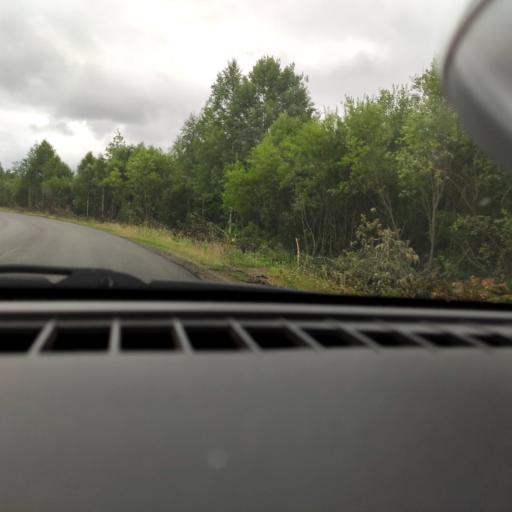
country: RU
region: Perm
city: Polazna
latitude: 58.3358
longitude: 56.1879
